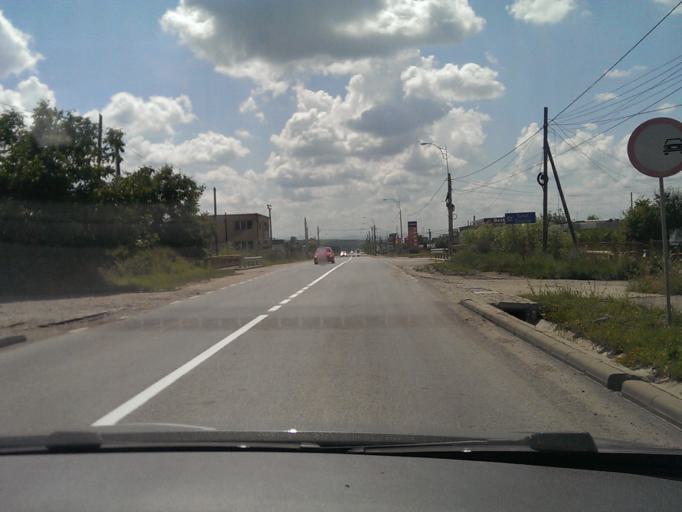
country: RO
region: Cluj
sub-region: Comuna Apahida
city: Sannicoara
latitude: 46.7912
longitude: 23.7397
